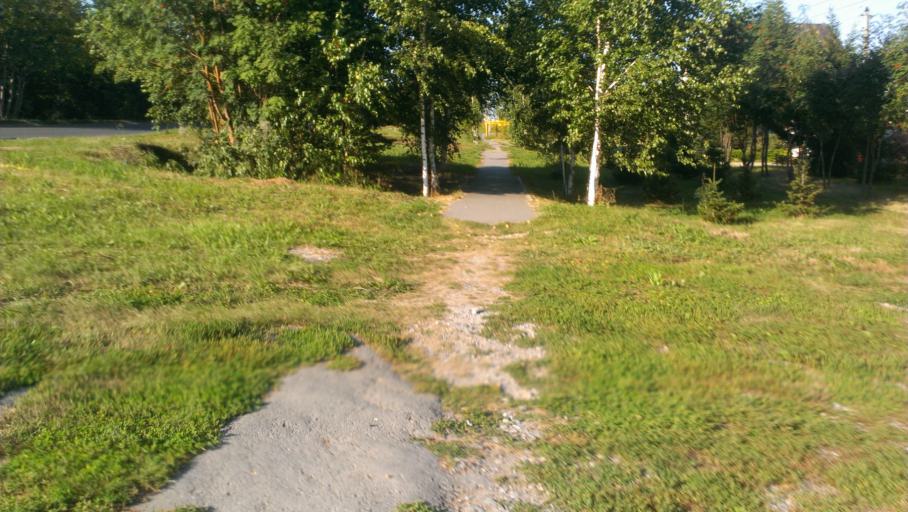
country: RU
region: Altai Krai
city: Novosilikatnyy
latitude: 53.3626
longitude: 83.6434
